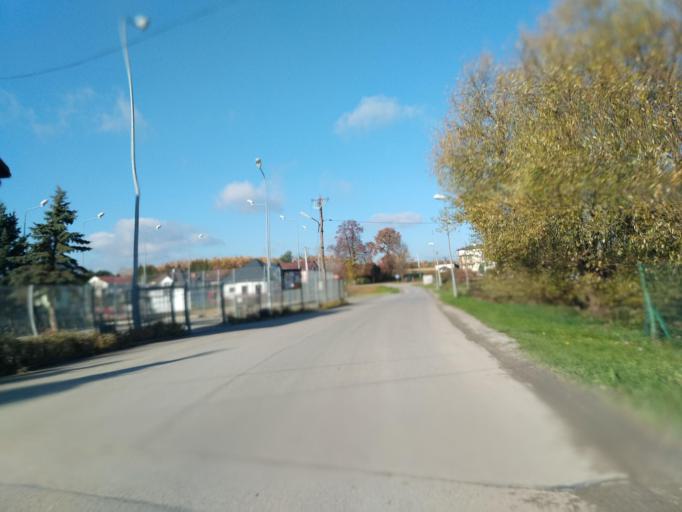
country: PL
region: Subcarpathian Voivodeship
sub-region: Powiat rzeszowski
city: Niechobrz
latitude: 50.0099
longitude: 21.8955
